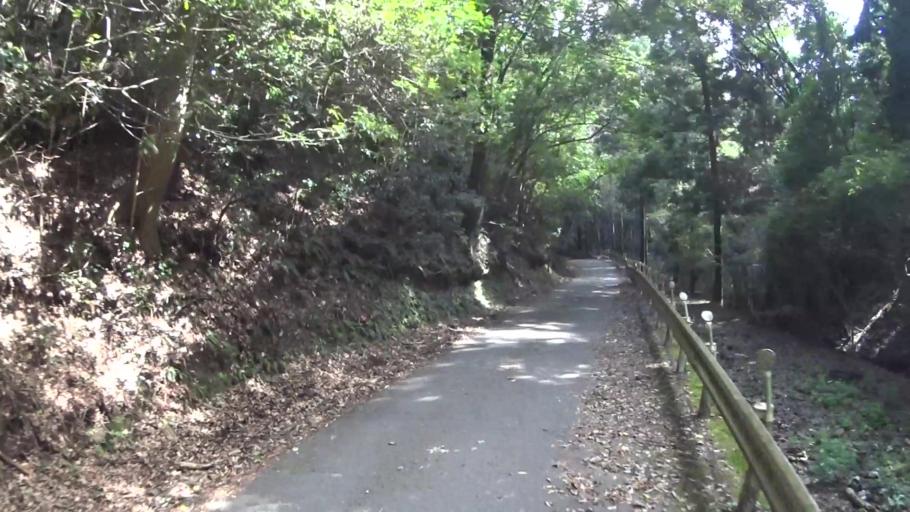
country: JP
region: Shiga Prefecture
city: Otsu-shi
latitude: 34.9440
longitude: 135.8713
